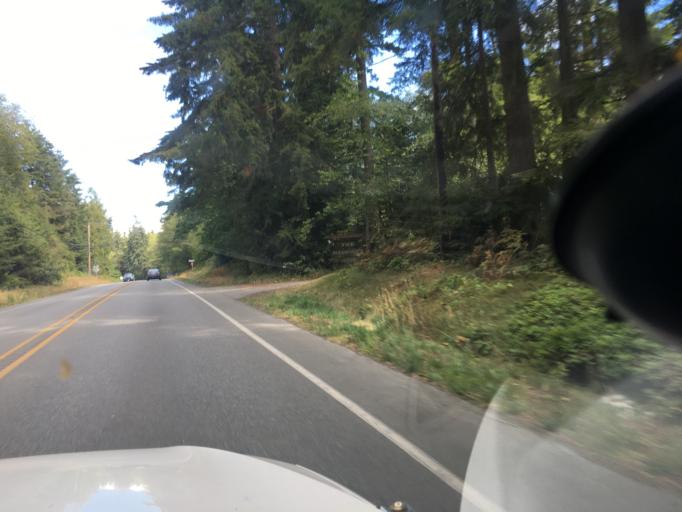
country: US
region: Washington
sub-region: Kitsap County
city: Kingston
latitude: 47.8053
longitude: -122.5650
